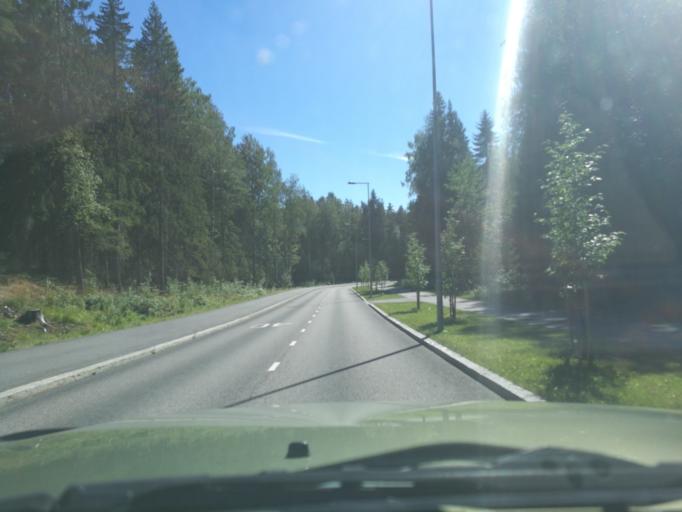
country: FI
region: Uusimaa
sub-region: Helsinki
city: Kerava
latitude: 60.3537
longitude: 25.1372
